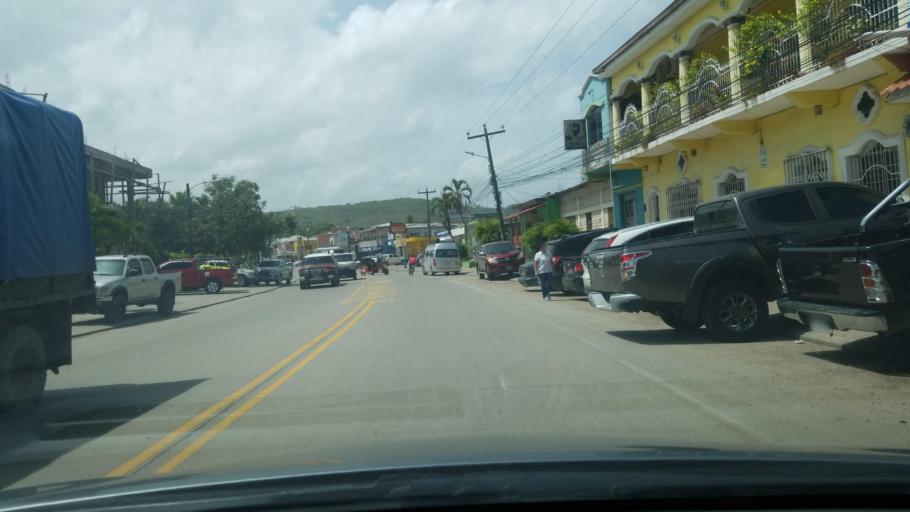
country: HN
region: Copan
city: La Entrada
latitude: 15.0626
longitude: -88.7570
